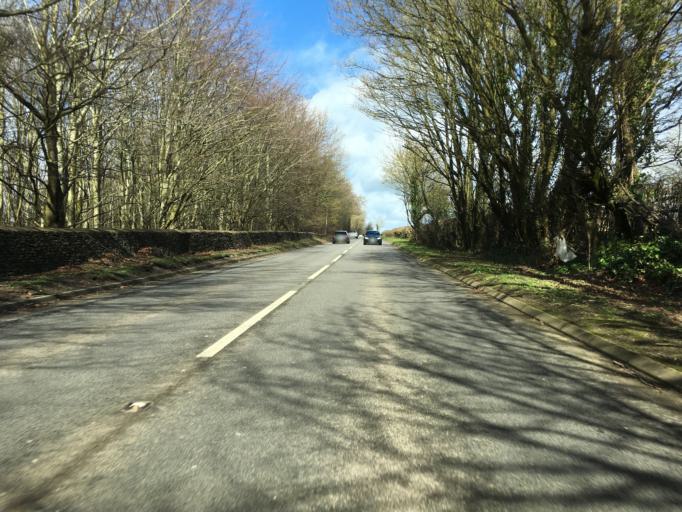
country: GB
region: England
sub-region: South Gloucestershire
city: Horton
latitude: 51.5133
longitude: -2.3436
